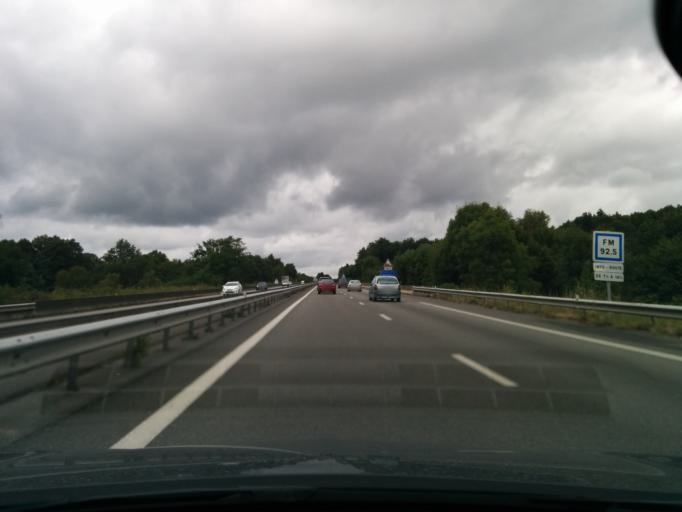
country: FR
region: Limousin
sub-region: Departement de la Haute-Vienne
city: Bessines-sur-Gartempe
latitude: 46.0766
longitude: 1.3582
